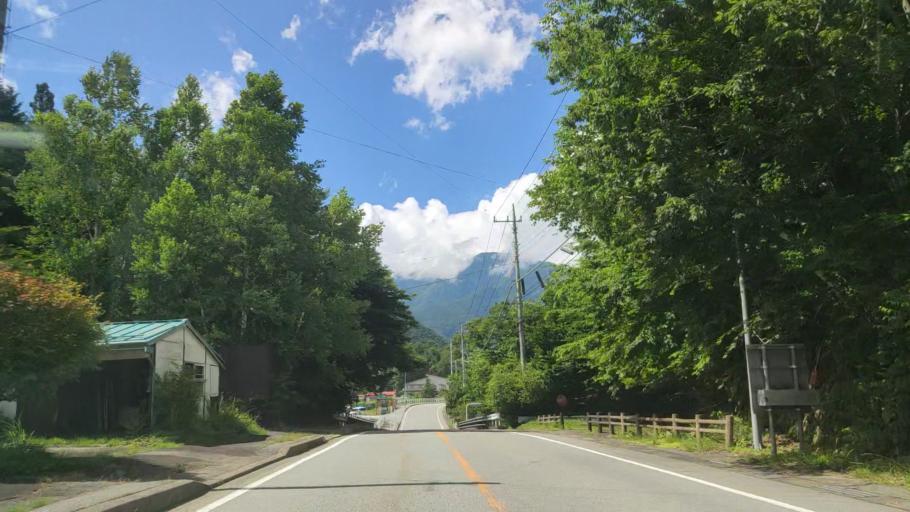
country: JP
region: Yamanashi
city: Enzan
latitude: 35.8491
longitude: 138.7602
